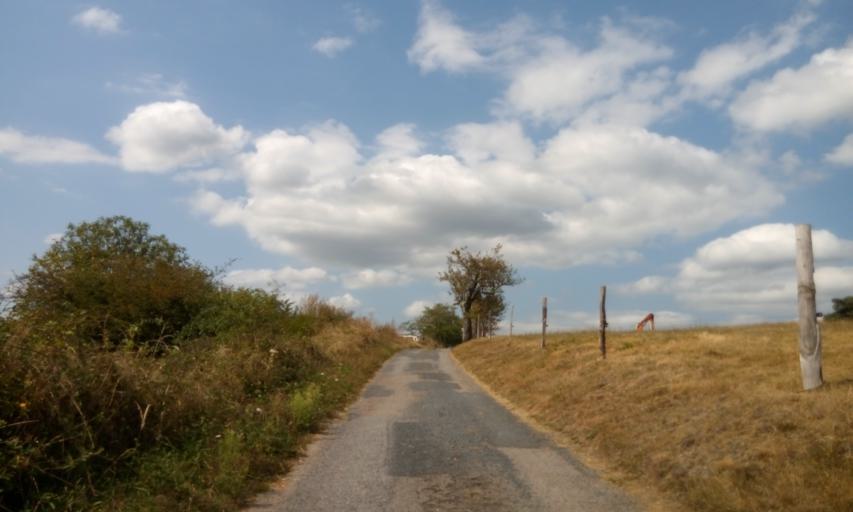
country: FR
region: Rhone-Alpes
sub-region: Departement du Rhone
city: Grandris
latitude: 46.0067
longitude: 4.4793
